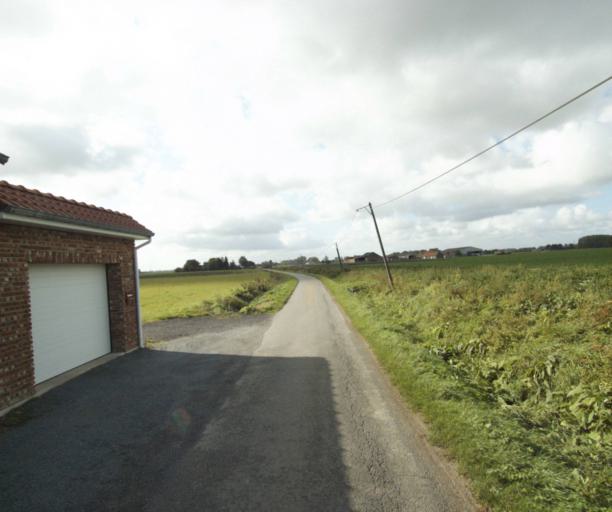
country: FR
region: Nord-Pas-de-Calais
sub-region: Departement du Nord
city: Perenchies
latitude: 50.6912
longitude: 2.9501
